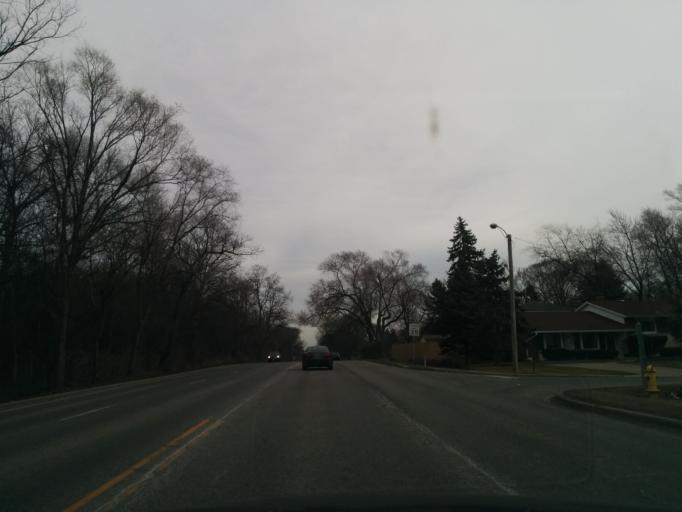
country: US
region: Illinois
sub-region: Cook County
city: Western Springs
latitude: 41.8201
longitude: -87.8947
